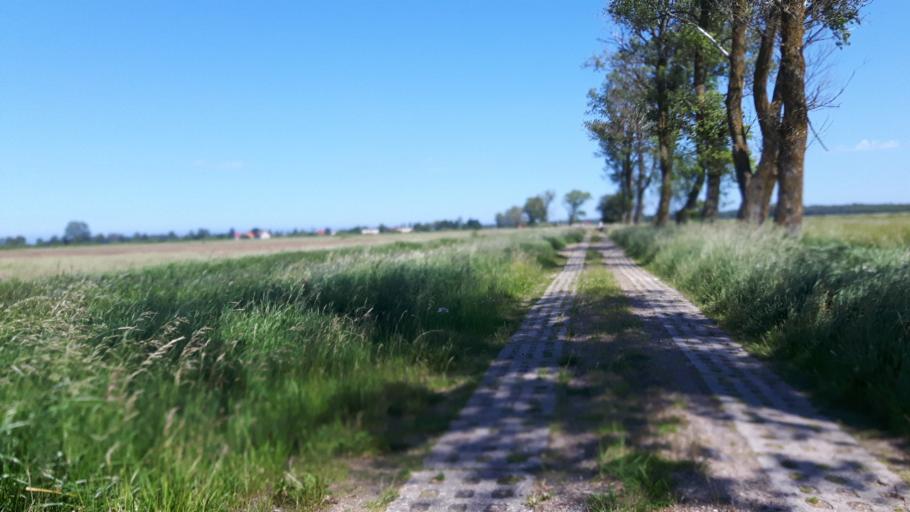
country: PL
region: Pomeranian Voivodeship
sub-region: Powiat slupski
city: Smoldzino
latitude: 54.6789
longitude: 17.2704
